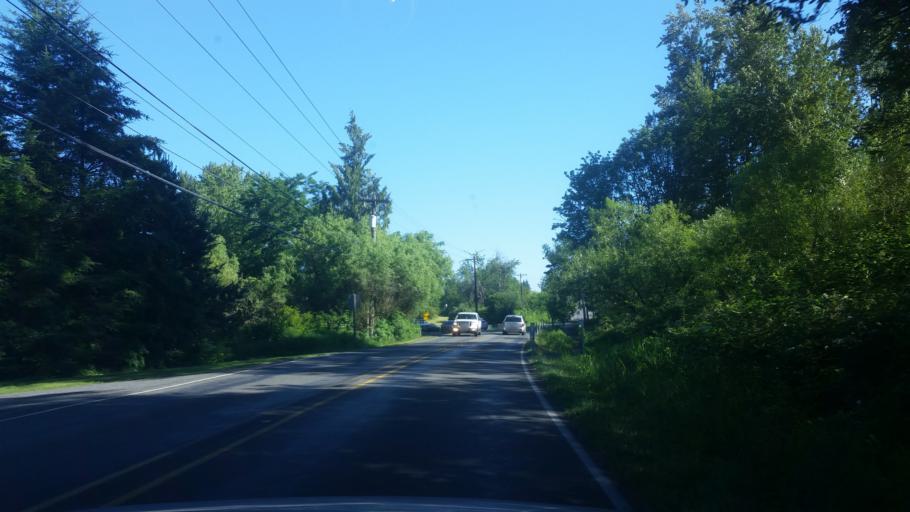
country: US
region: Washington
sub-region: Snohomish County
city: Cathcart
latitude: 47.8702
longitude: -122.0993
